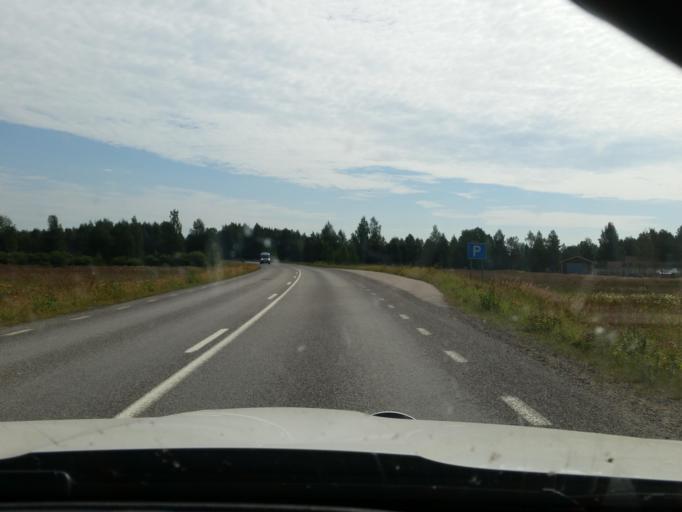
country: SE
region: Norrbotten
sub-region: Alvsbyns Kommun
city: AElvsbyn
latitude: 65.6923
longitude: 20.6034
